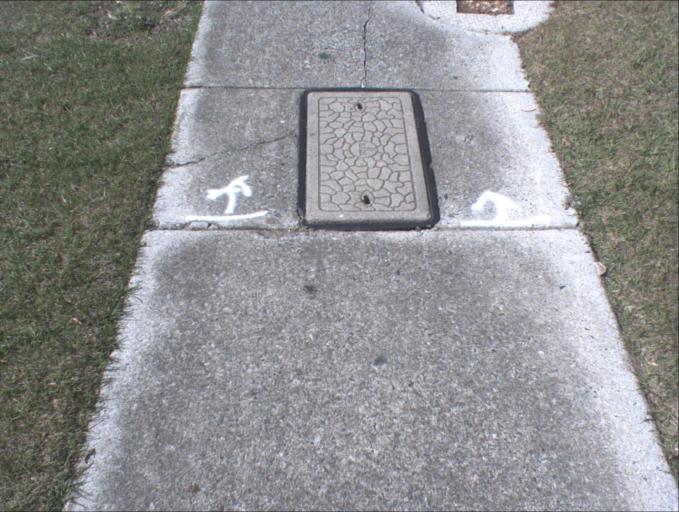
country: AU
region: Queensland
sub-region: Logan
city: Park Ridge South
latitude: -27.6934
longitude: 153.0192
